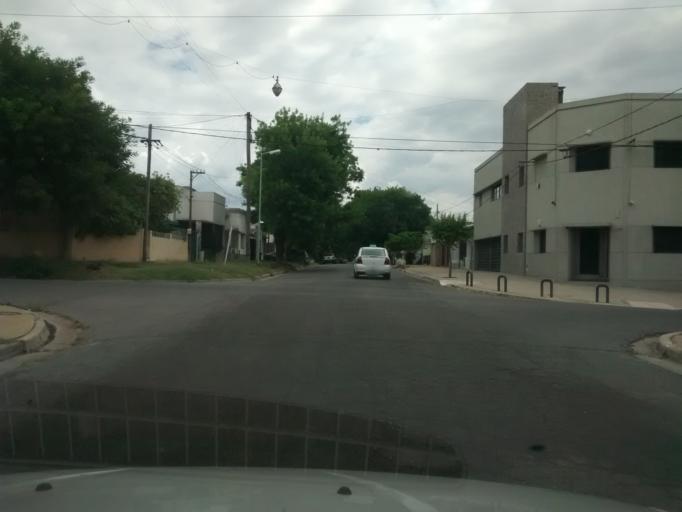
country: AR
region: Buenos Aires
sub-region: Partido de La Plata
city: La Plata
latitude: -34.9298
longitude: -57.9224
